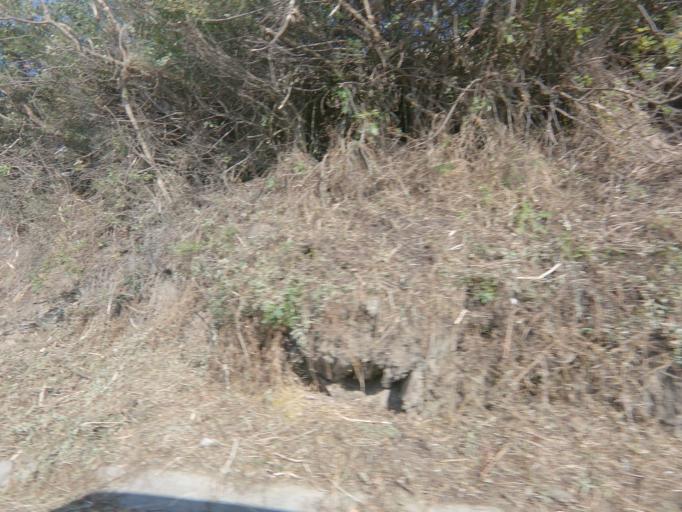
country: PT
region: Vila Real
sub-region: Sabrosa
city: Vilela
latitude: 41.2217
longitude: -7.5554
